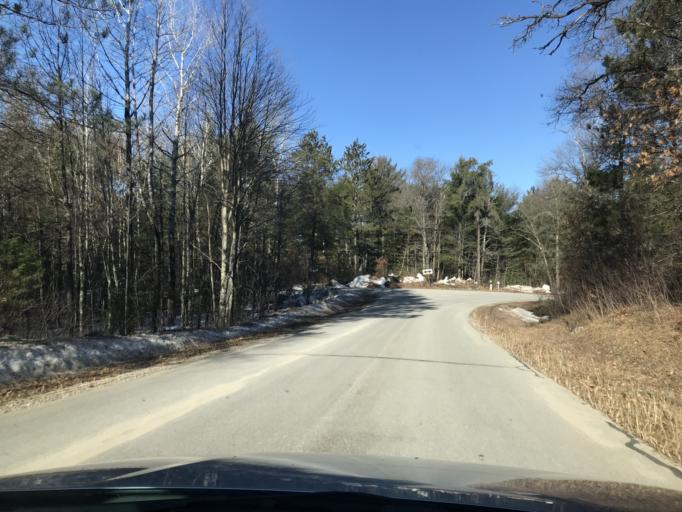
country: US
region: Wisconsin
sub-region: Marinette County
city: Niagara
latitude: 45.3907
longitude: -88.0780
